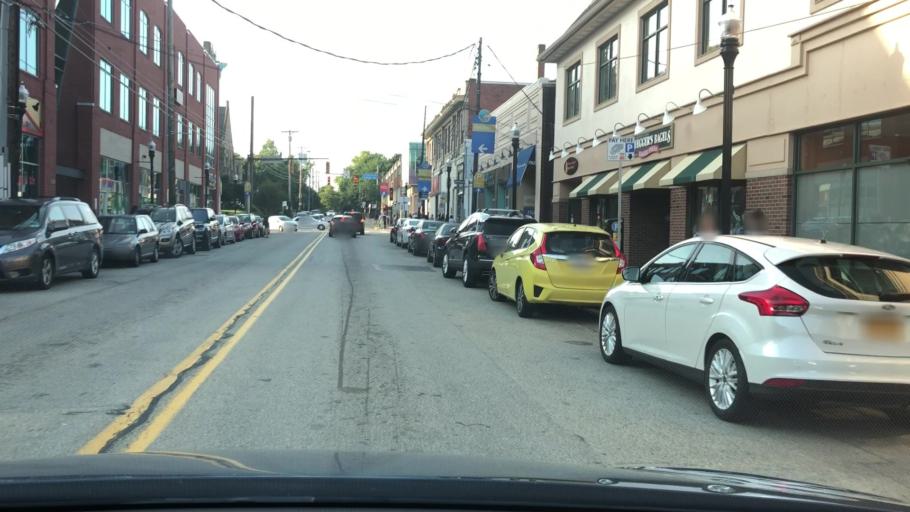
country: US
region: Pennsylvania
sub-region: Allegheny County
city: Homestead
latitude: 40.4373
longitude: -79.9230
